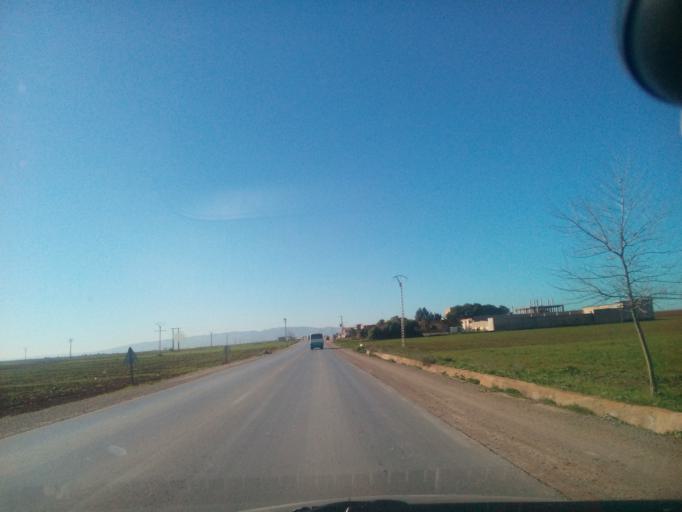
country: DZ
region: Relizane
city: Djidiouia
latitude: 35.8947
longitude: 0.6629
